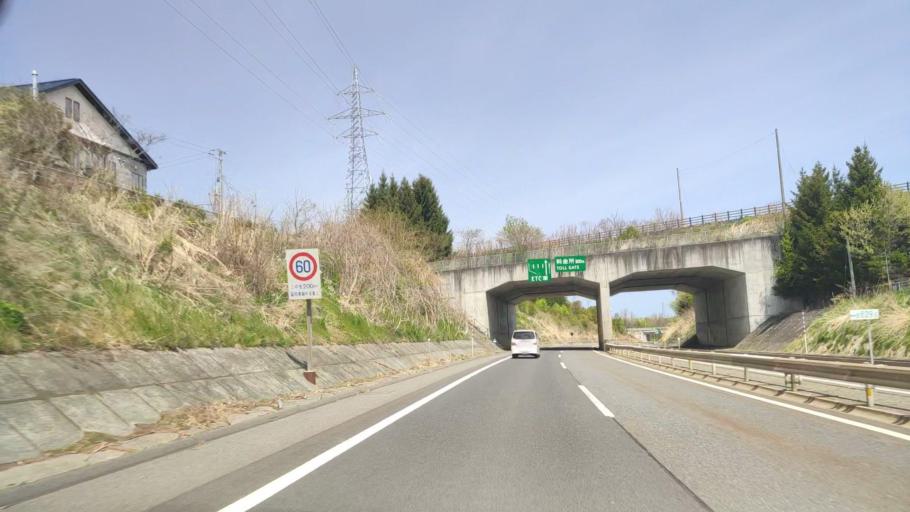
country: JP
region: Aomori
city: Hachinohe
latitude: 40.4782
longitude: 141.4594
